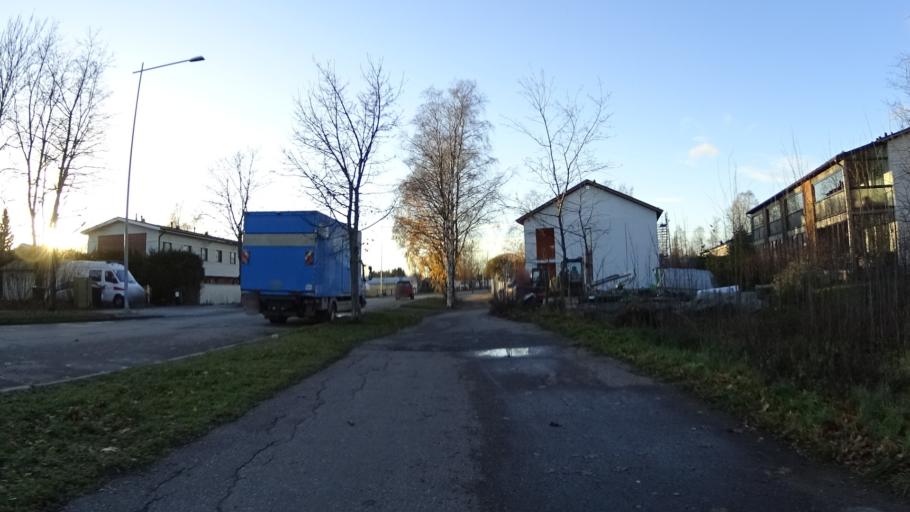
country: FI
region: Uusimaa
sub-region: Helsinki
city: Vantaa
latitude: 60.2977
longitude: 25.0247
